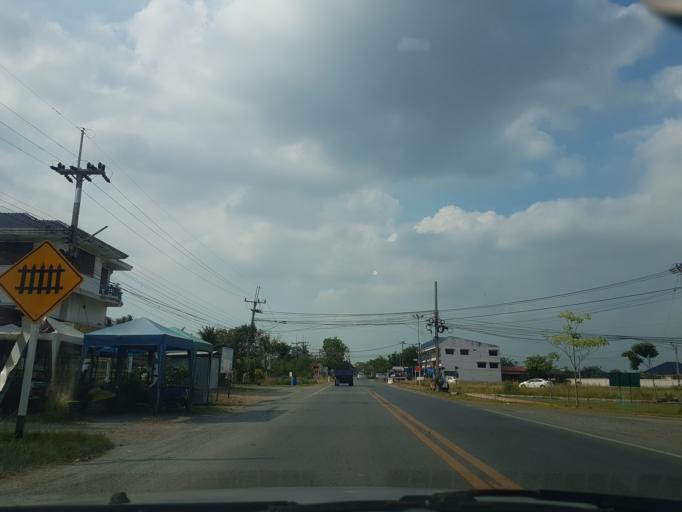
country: TH
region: Phra Nakhon Si Ayutthaya
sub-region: Amphoe Tha Ruea
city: Tha Ruea
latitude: 14.5516
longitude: 100.7265
